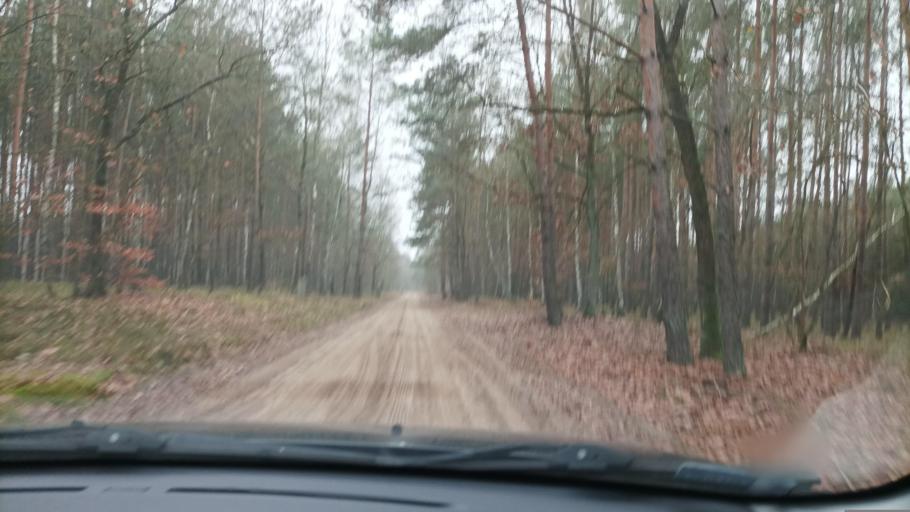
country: PL
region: Greater Poland Voivodeship
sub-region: Powiat czarnkowsko-trzcianecki
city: Polajewo
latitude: 52.7514
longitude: 16.7577
